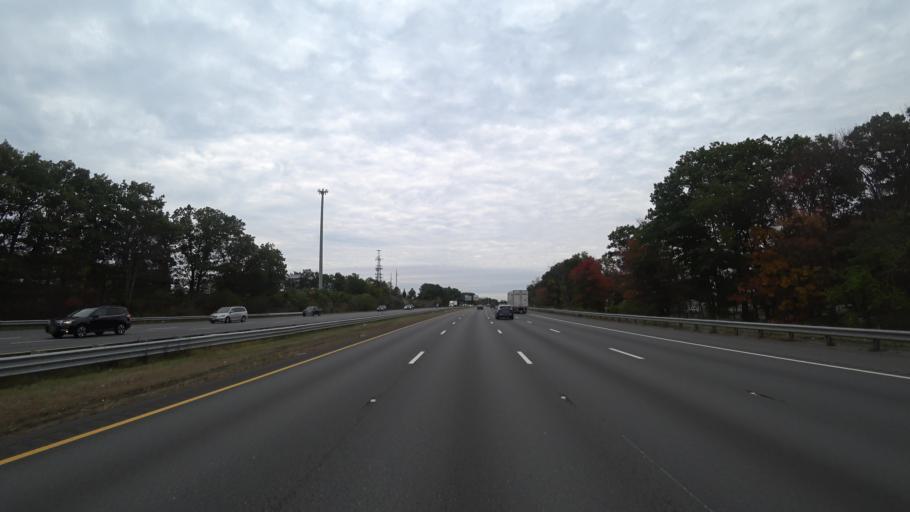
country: US
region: Massachusetts
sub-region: Middlesex County
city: Reading
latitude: 42.5273
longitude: -71.1359
